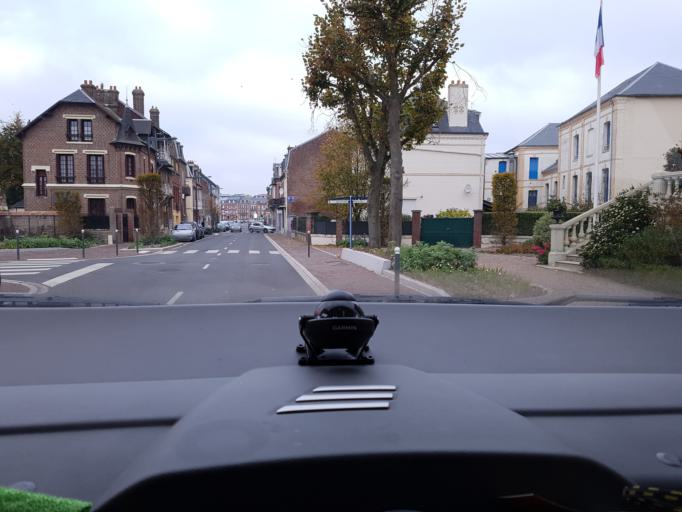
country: FR
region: Picardie
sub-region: Departement de la Somme
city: Mers-les-Bains
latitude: 50.0657
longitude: 1.3895
